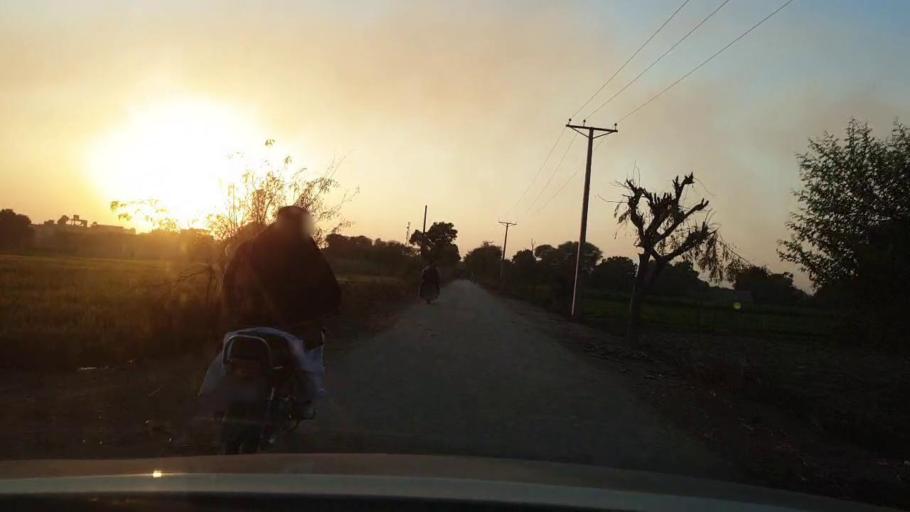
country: PK
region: Sindh
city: Tando Allahyar
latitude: 25.5239
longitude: 68.6231
